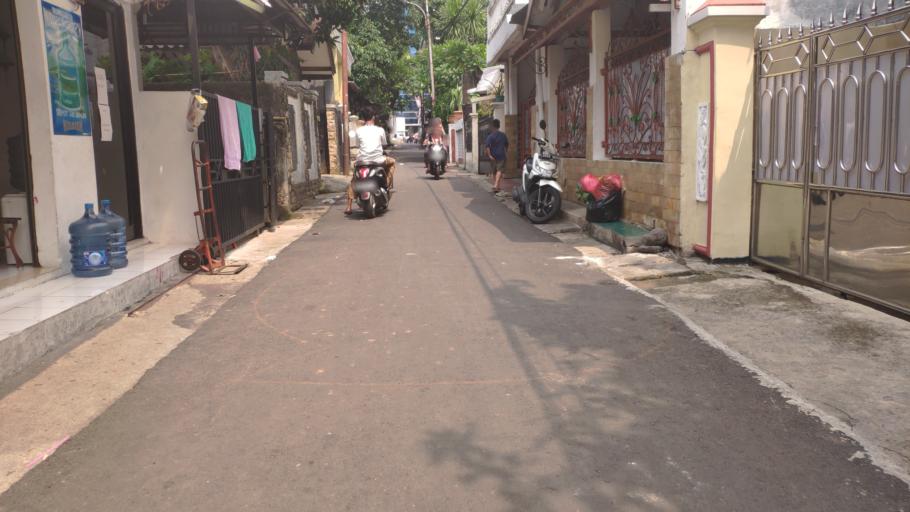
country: ID
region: Jakarta Raya
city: Jakarta
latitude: -6.2652
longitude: 106.8297
